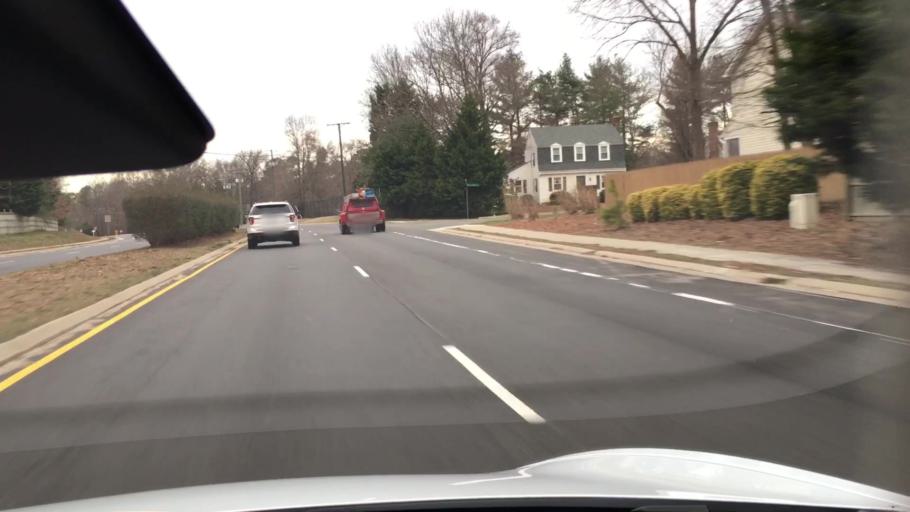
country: US
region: Virginia
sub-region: Chesterfield County
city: Bon Air
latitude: 37.5150
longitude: -77.5919
